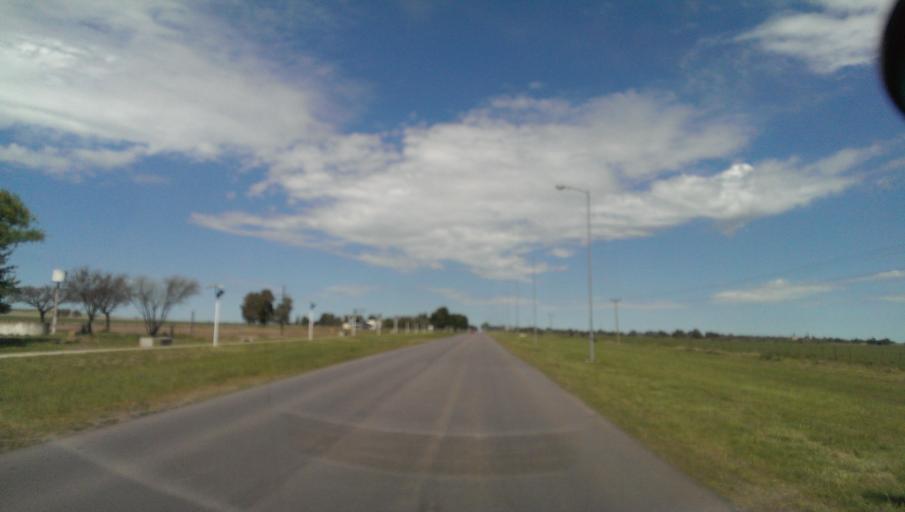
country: AR
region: Buenos Aires
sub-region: Partido de Tornquist
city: Tornquist
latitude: -38.0724
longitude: -62.2209
